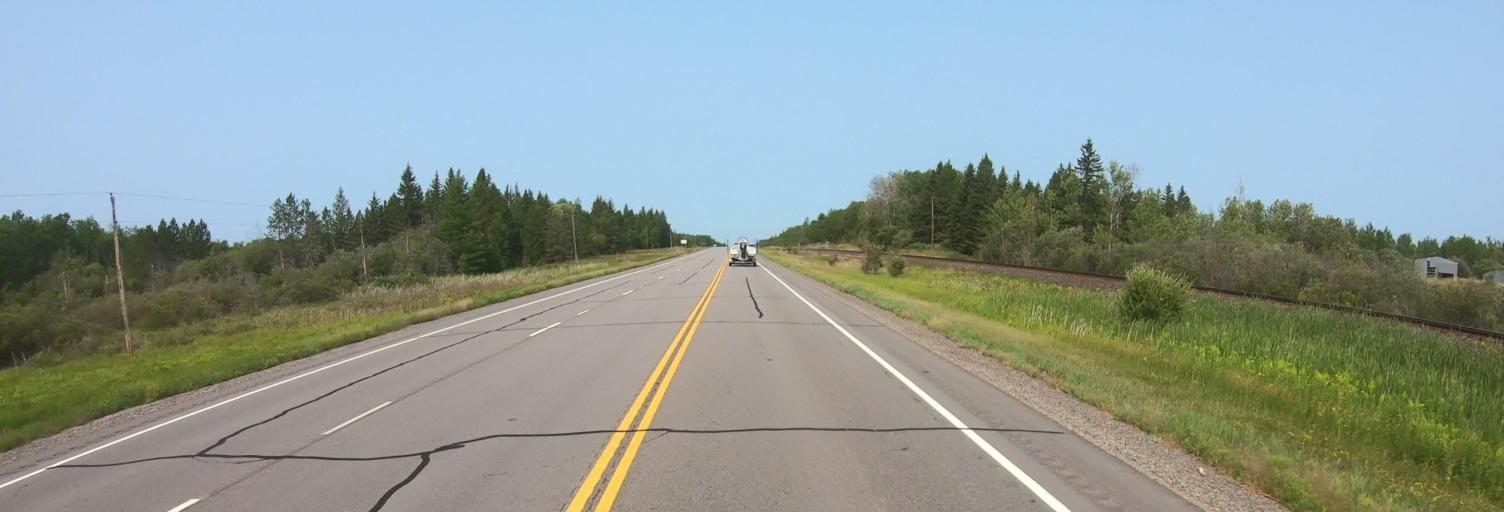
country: CA
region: Ontario
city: Fort Frances
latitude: 48.4436
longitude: -93.2601
